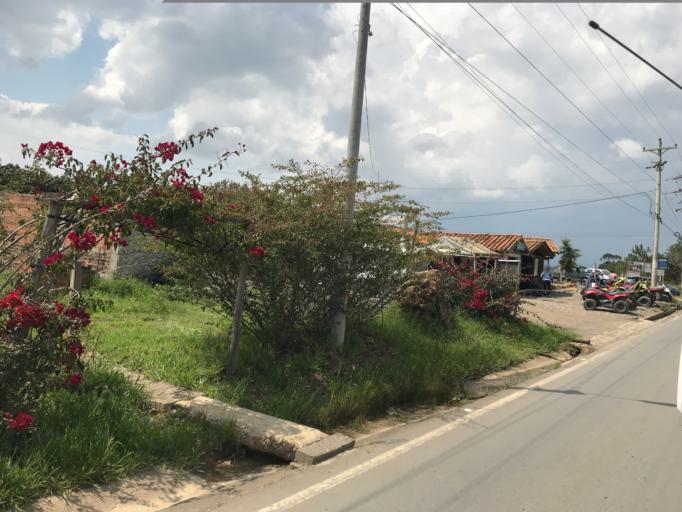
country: CO
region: Boyaca
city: Sachica
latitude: 5.6179
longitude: -73.5342
